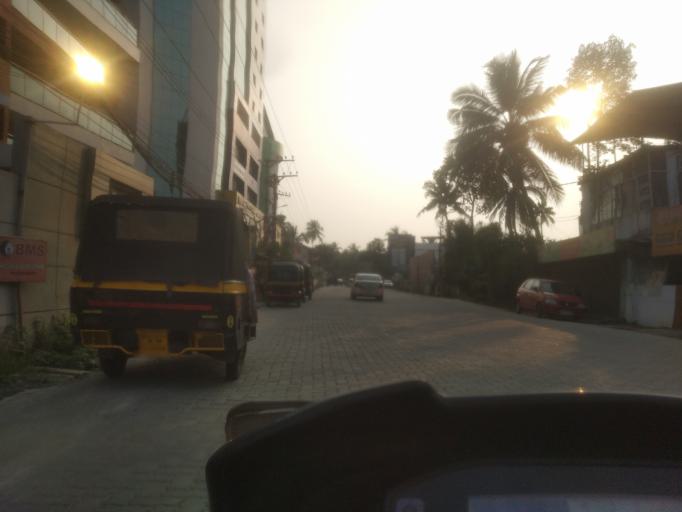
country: IN
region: Kerala
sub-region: Ernakulam
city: Cochin
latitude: 9.9405
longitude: 76.3315
